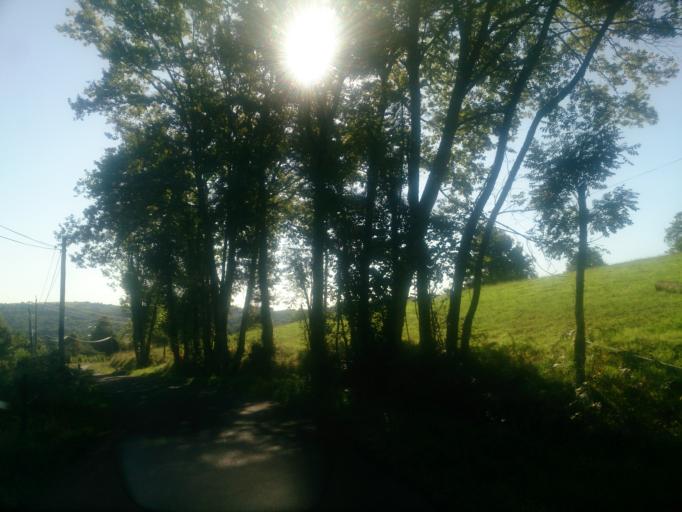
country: FR
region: Midi-Pyrenees
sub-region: Departement des Hautes-Pyrenees
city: Horgues
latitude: 43.1334
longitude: 0.0945
